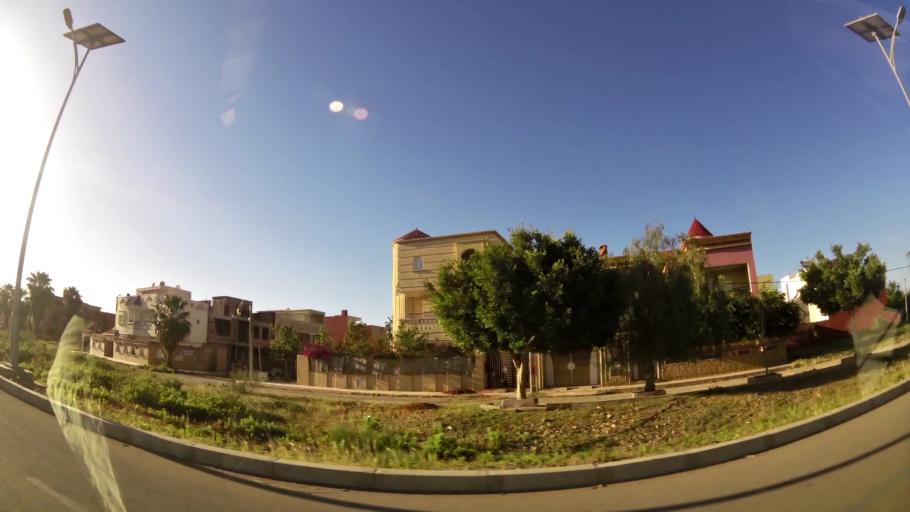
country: MA
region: Oriental
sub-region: Berkane-Taourirt
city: Madagh
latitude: 35.0820
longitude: -2.2470
